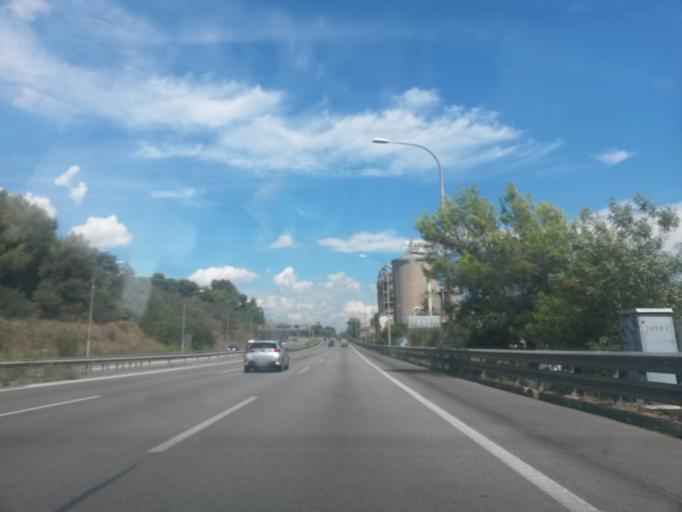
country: ES
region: Catalonia
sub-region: Provincia de Barcelona
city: Montcada i Reixac
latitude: 41.4715
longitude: 2.1793
